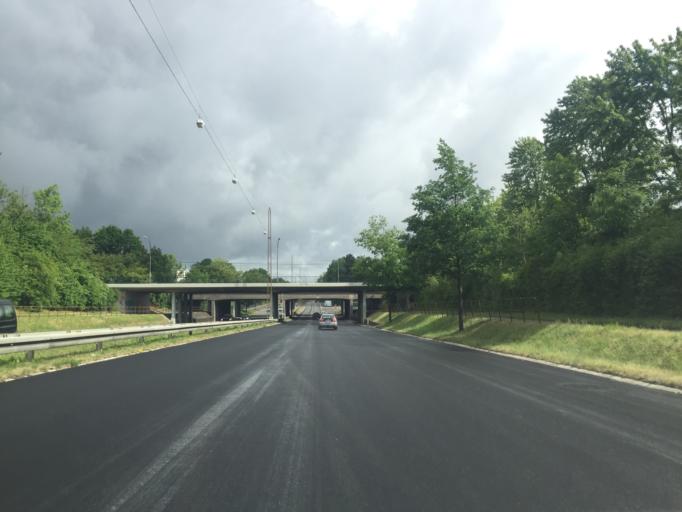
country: DK
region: Capital Region
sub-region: Rodovre Kommune
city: Rodovre
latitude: 55.6635
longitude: 12.4552
